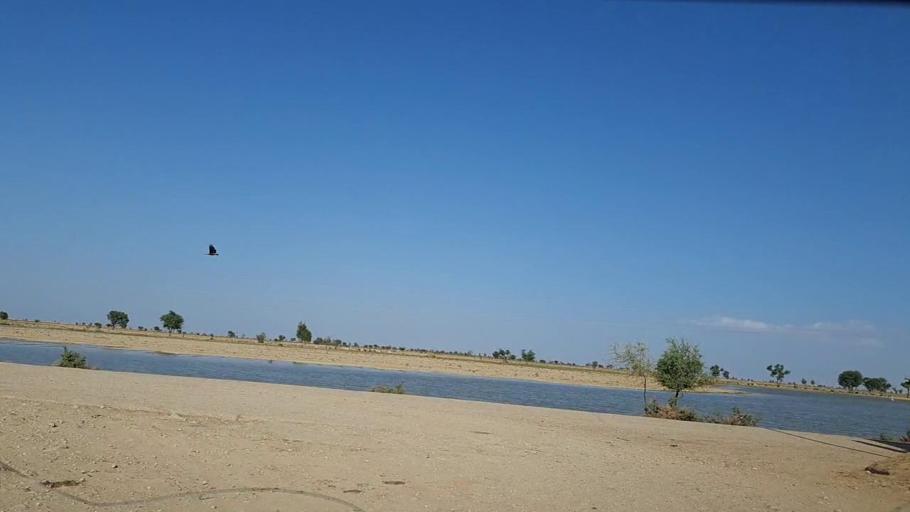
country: PK
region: Sindh
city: Johi
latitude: 26.5309
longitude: 67.5329
